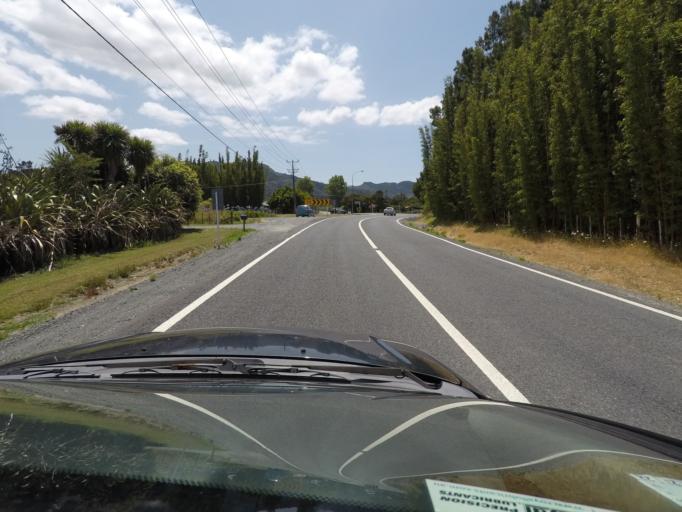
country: NZ
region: Auckland
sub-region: Auckland
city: Warkworth
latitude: -36.3232
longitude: 174.7311
